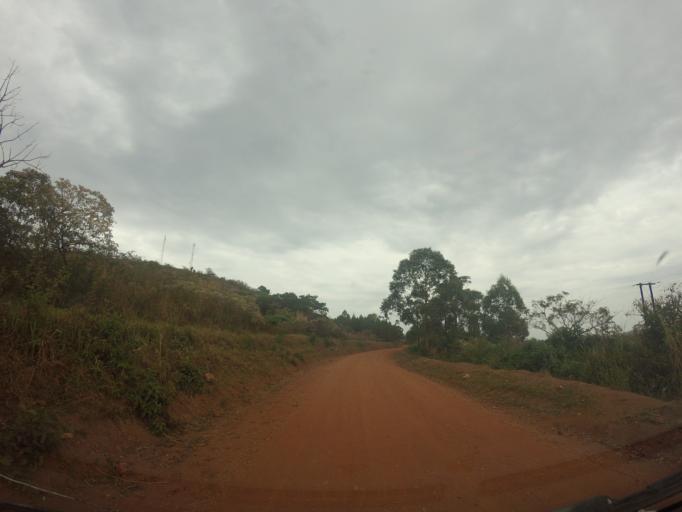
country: UG
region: Northern Region
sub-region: Zombo District
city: Zombo
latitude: 2.7637
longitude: 30.8545
